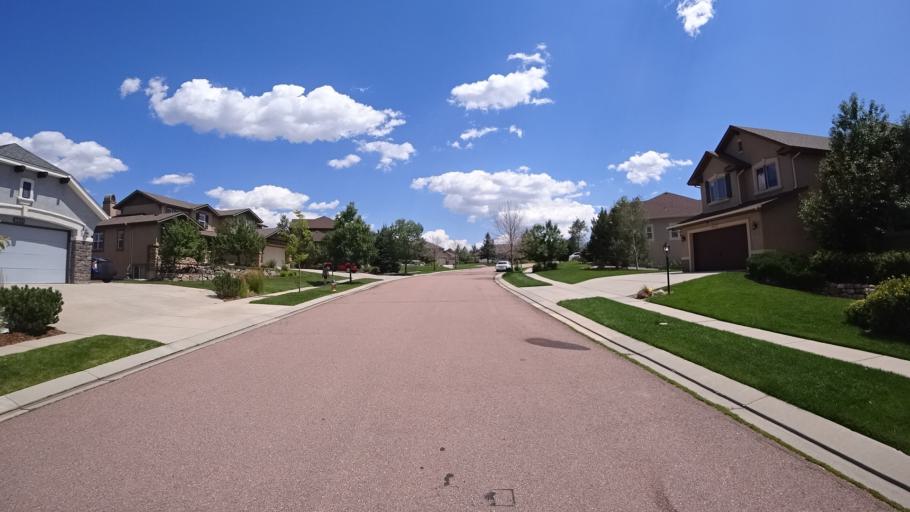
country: US
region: Colorado
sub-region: El Paso County
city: Black Forest
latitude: 38.9712
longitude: -104.7604
